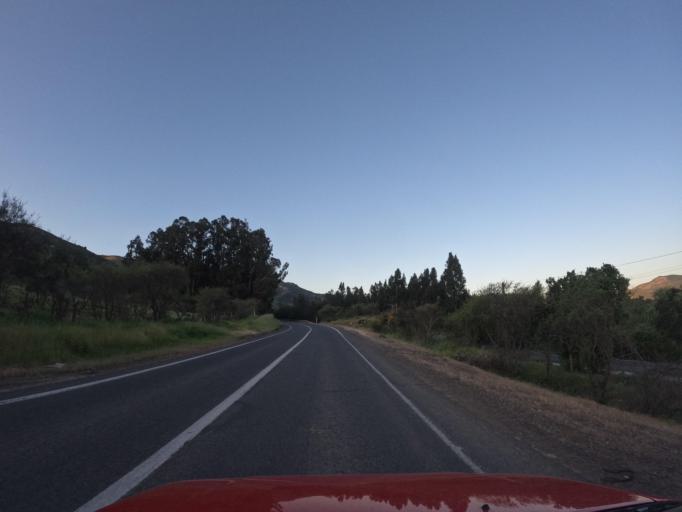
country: CL
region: Maule
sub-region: Provincia de Curico
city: Rauco
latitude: -35.0727
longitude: -71.6259
